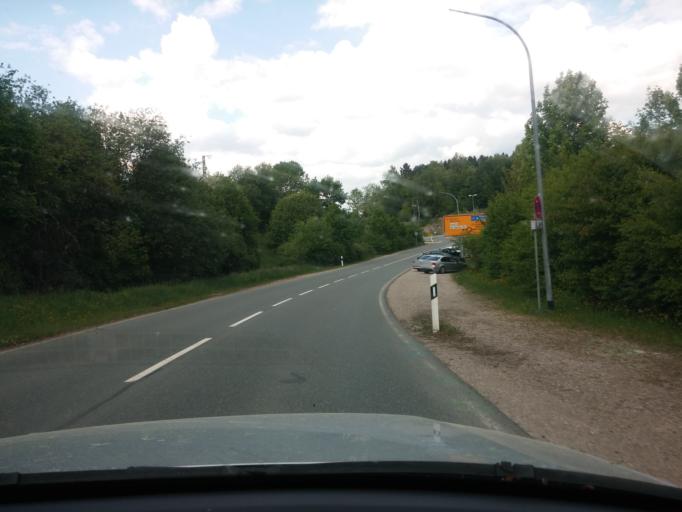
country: DE
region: Bavaria
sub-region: Upper Bavaria
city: Holzkirchen
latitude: 47.8854
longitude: 11.7136
